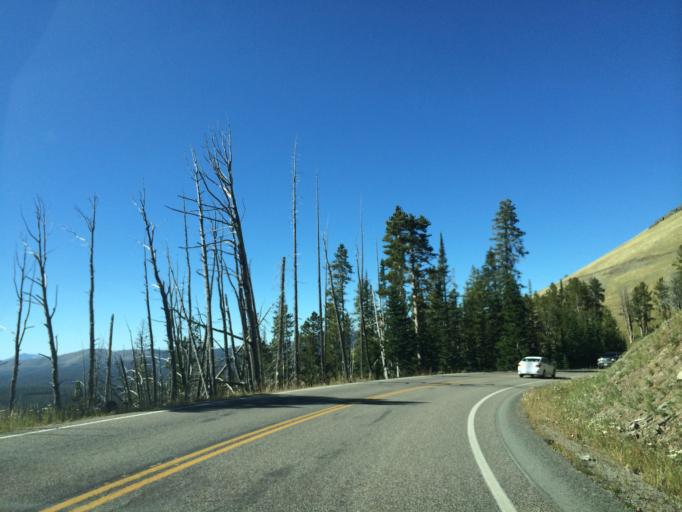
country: US
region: Montana
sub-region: Gallatin County
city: West Yellowstone
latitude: 44.8120
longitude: -110.4456
